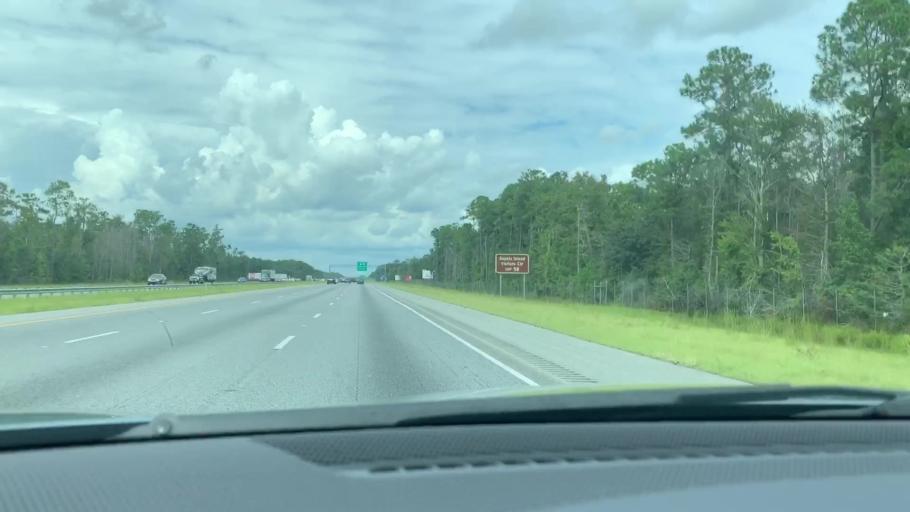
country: US
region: Georgia
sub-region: McIntosh County
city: Darien
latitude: 31.5167
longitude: -81.4456
